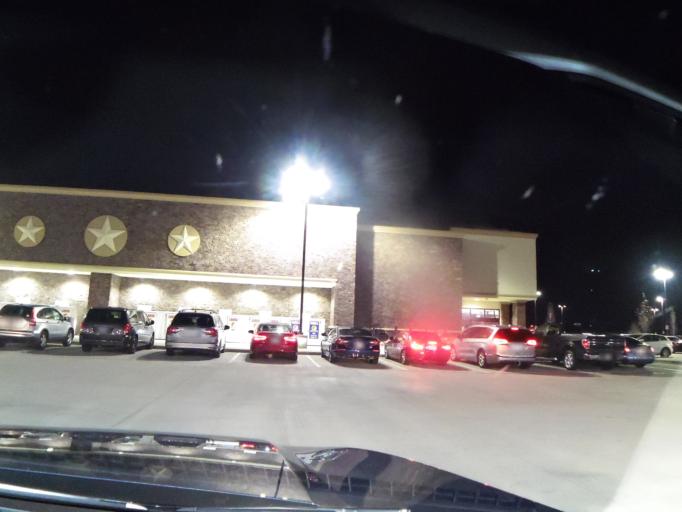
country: US
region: Georgia
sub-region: Houston County
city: Centerville
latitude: 32.5847
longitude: -83.7400
